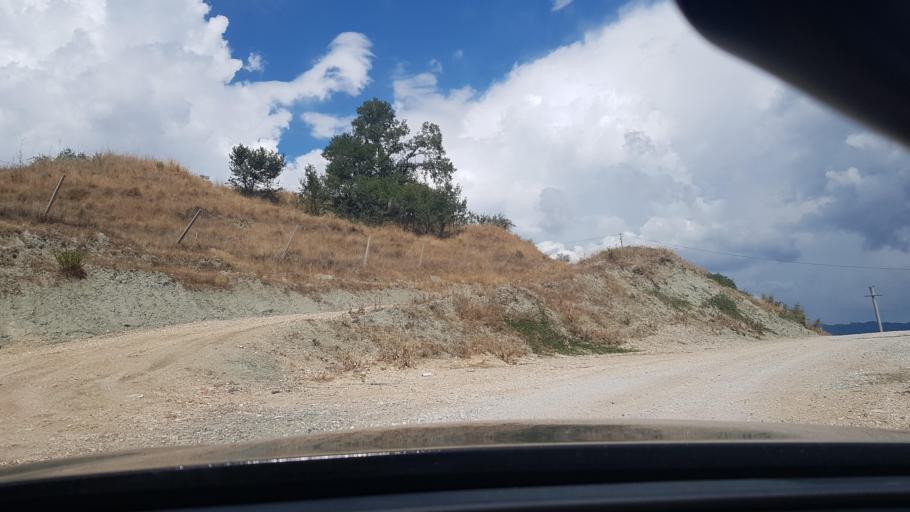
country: AL
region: Durres
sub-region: Rrethi i Durresit
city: Rrashbull
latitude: 41.2936
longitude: 19.5445
